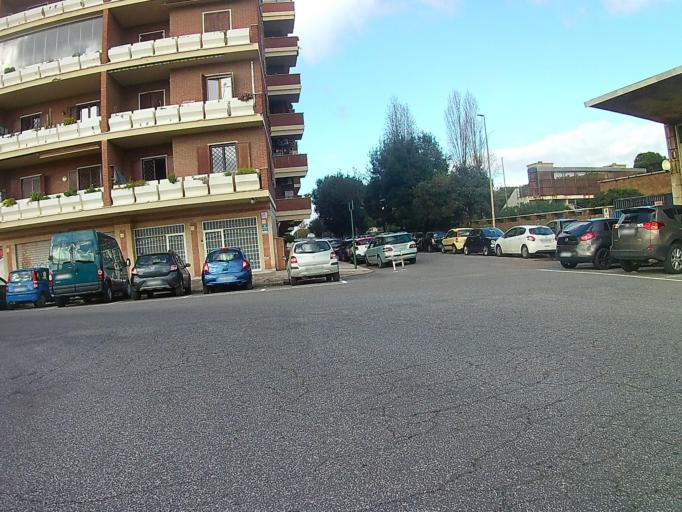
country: IT
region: Latium
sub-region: Citta metropolitana di Roma Capitale
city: Lido di Ostia
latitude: 41.7202
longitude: 12.3086
